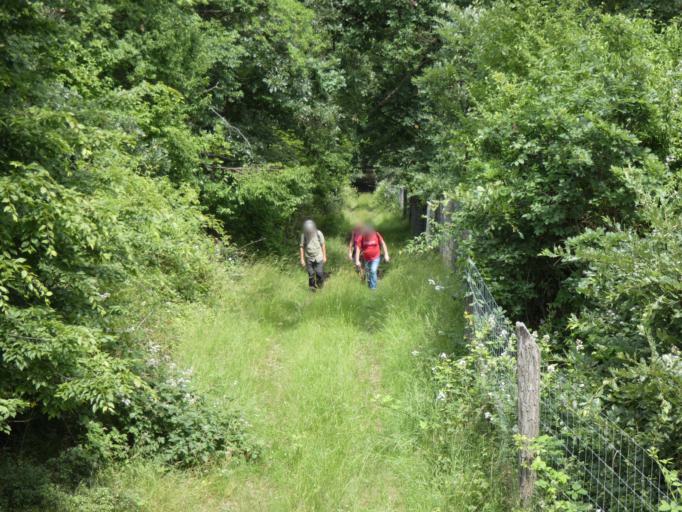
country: HU
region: Pest
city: Kismaros
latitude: 47.8404
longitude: 18.9645
